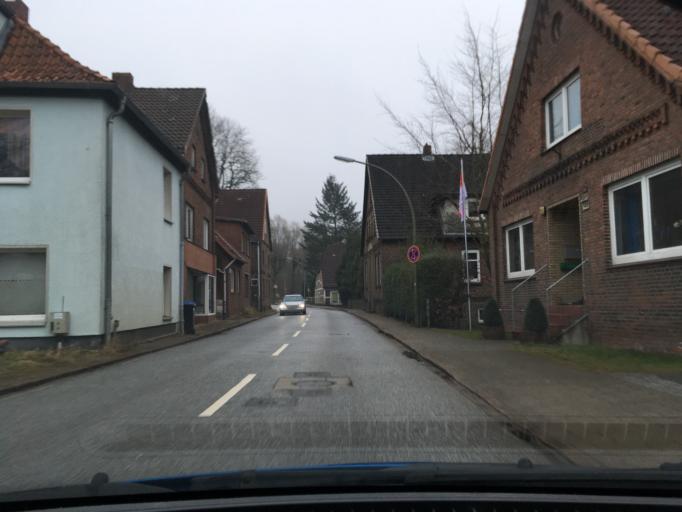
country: DE
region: Hamburg
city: Harburg
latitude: 53.4895
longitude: 9.9380
